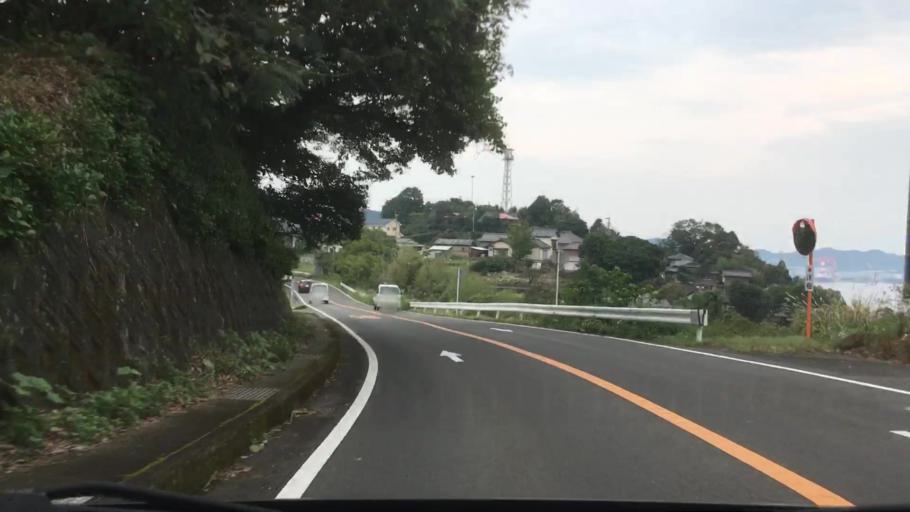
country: JP
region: Nagasaki
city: Sasebo
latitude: 33.0390
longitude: 129.6726
